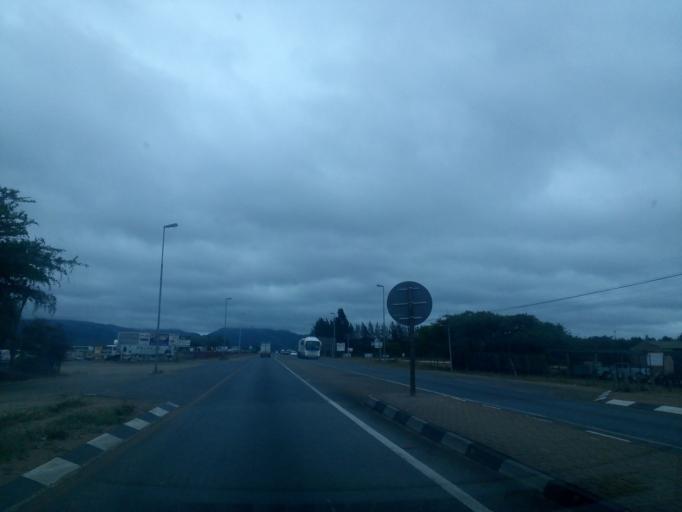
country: ZA
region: Limpopo
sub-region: Vhembe District Municipality
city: Louis Trichardt
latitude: -23.0777
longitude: 29.9088
